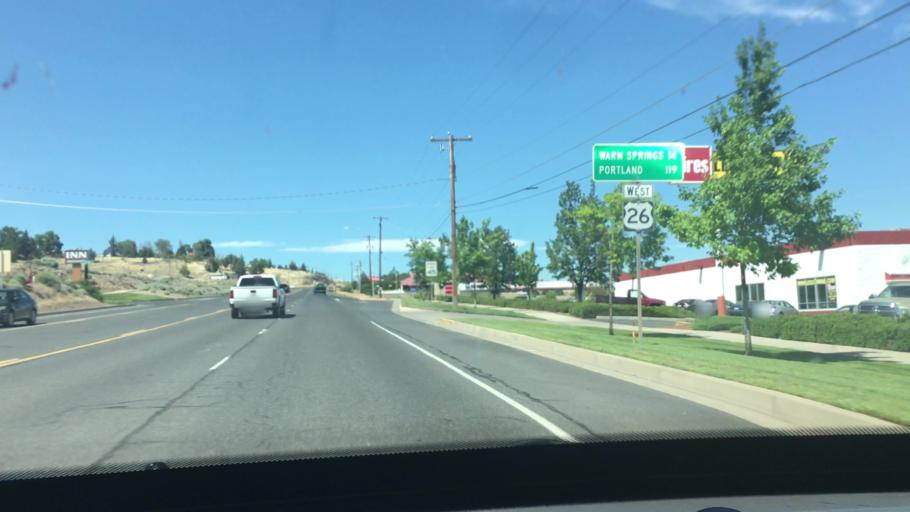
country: US
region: Oregon
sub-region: Jefferson County
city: Madras
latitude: 44.6422
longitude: -121.1295
